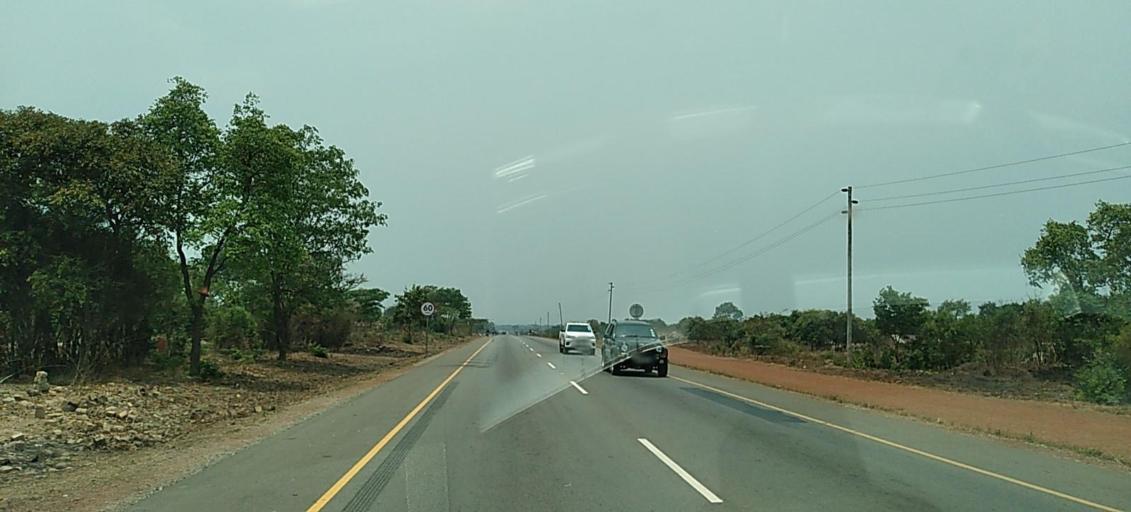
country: ZM
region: Copperbelt
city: Chililabombwe
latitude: -12.3773
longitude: 27.3151
